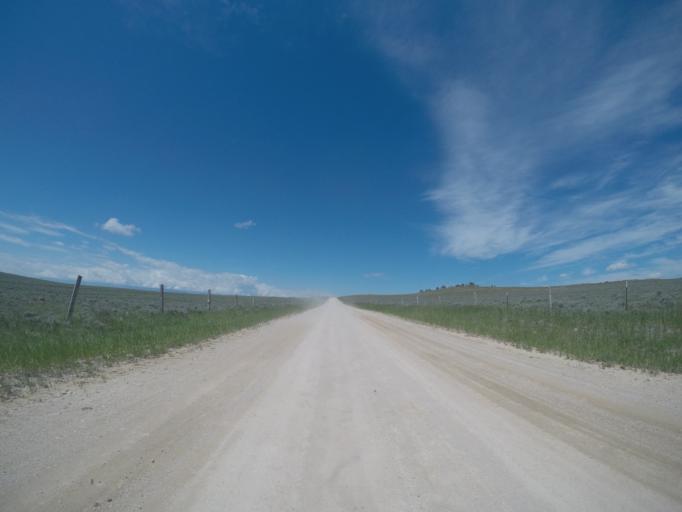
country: US
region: Wyoming
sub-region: Park County
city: Powell
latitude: 45.2055
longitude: -108.7621
